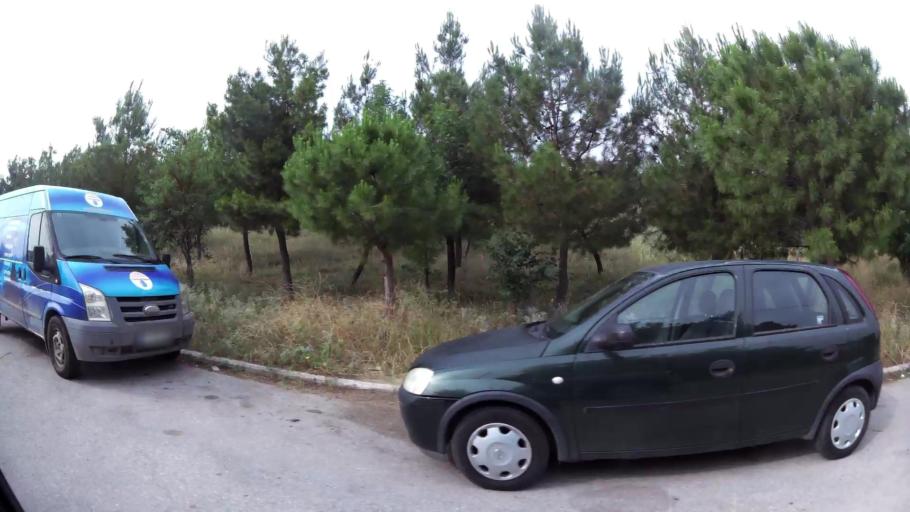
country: GR
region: Central Macedonia
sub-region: Nomos Thessalonikis
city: Oraiokastro
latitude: 40.7301
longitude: 22.9248
